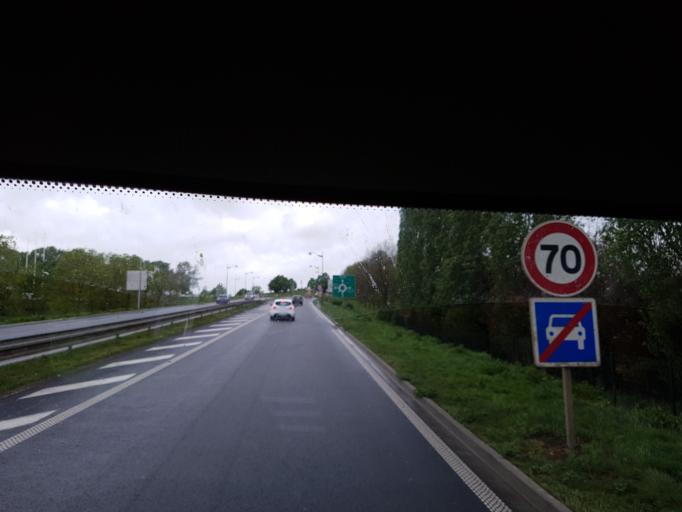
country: FR
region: Picardie
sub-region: Departement de l'Aisne
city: Courmelles
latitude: 49.3643
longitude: 3.3123
